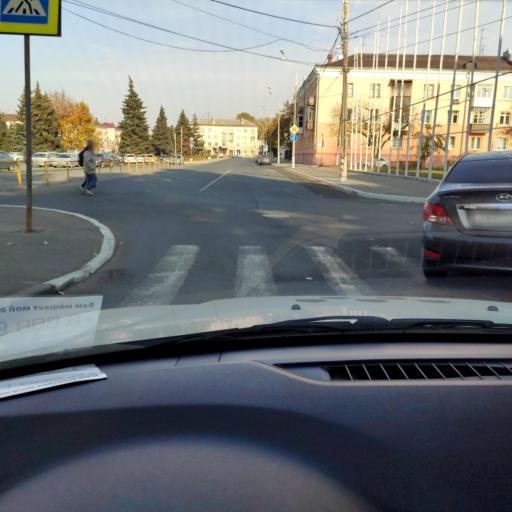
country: RU
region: Samara
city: Tol'yatti
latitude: 53.5122
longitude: 49.4081
